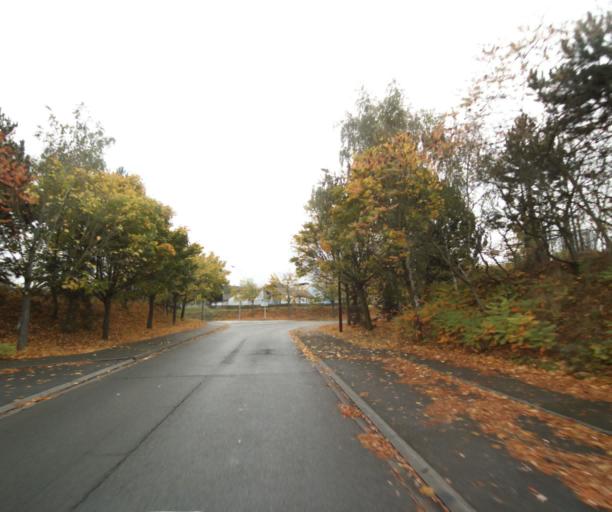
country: FR
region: Centre
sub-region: Departement d'Eure-et-Loir
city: Luray
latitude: 48.7406
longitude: 1.3901
